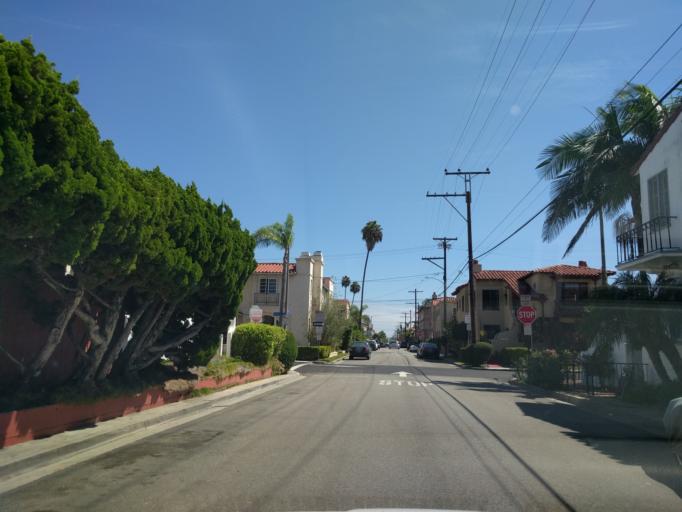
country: US
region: California
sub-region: Orange County
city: Seal Beach
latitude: 33.7604
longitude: -118.1408
